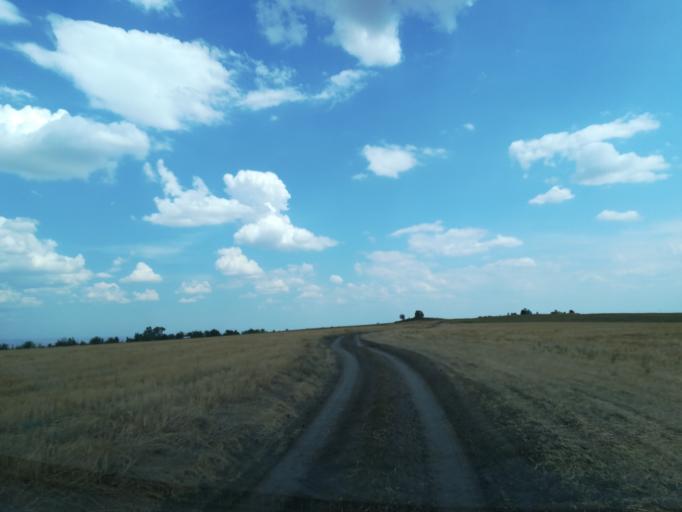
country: BG
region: Khaskovo
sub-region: Obshtina Mineralni Bani
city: Mineralni Bani
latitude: 42.0022
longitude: 25.1989
